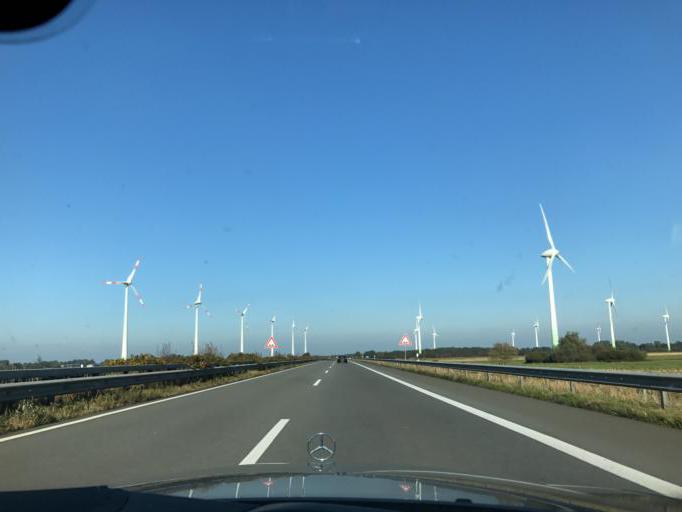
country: DE
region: Lower Saxony
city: Bunde
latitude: 53.1910
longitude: 7.3004
